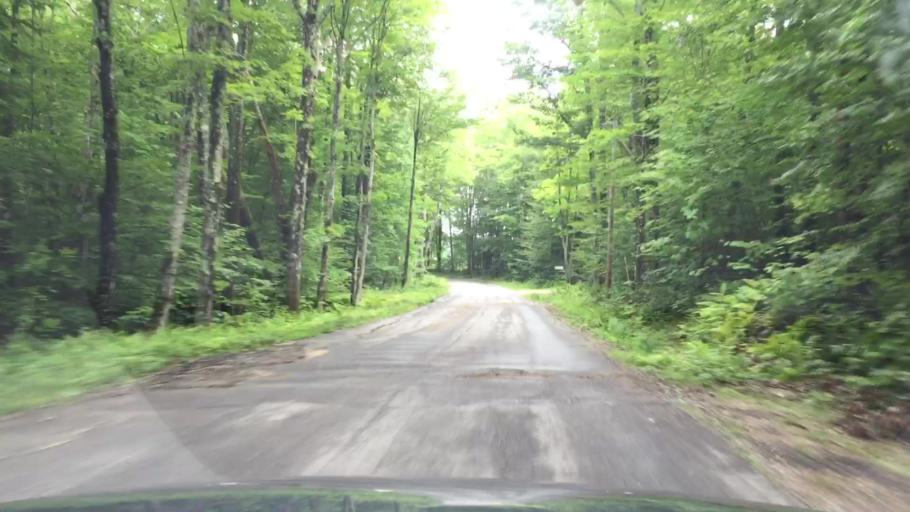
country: US
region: New Hampshire
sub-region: Carroll County
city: Sandwich
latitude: 43.7992
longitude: -71.4733
